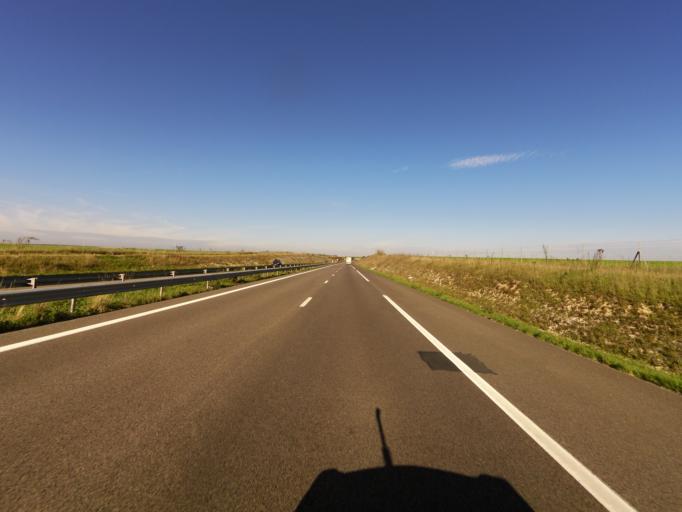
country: FR
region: Champagne-Ardenne
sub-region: Departement de la Marne
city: Fagnieres
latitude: 49.0263
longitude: 4.2871
